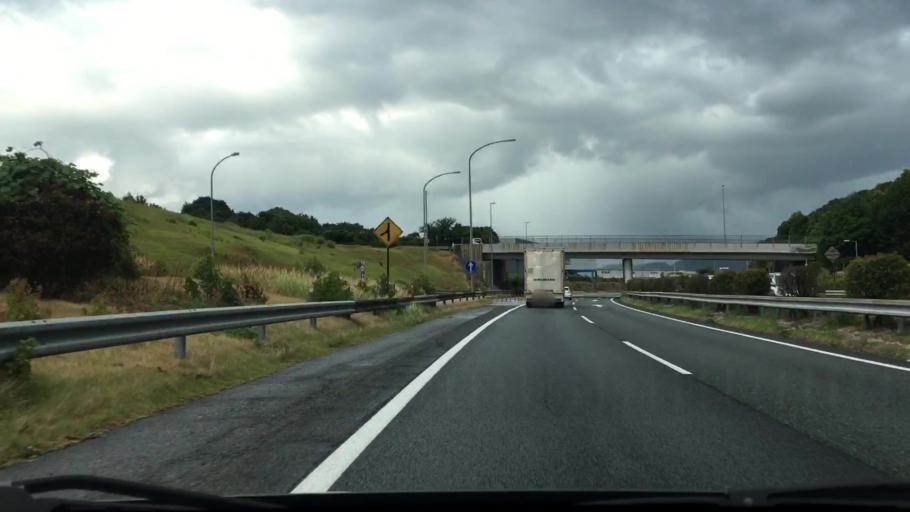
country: JP
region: Fukuoka
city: Miyata
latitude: 33.7475
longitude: 130.6078
